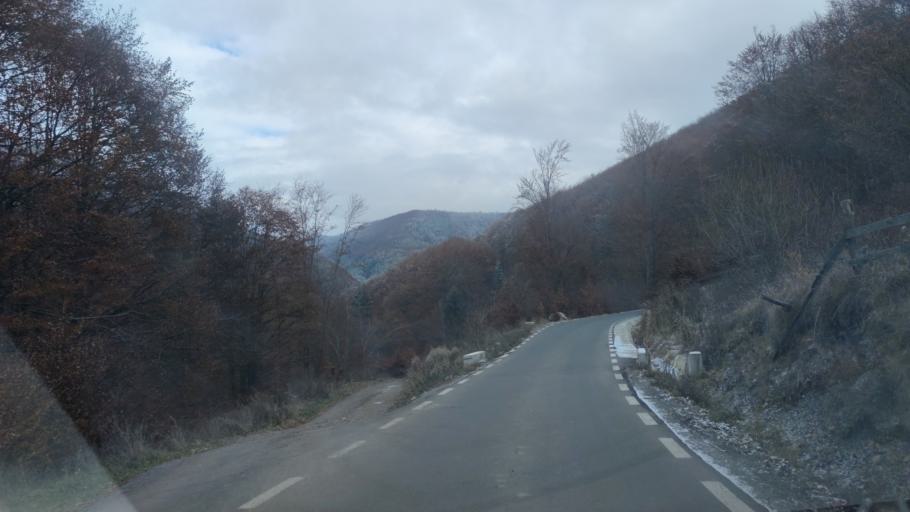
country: RO
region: Harghita
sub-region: Comuna Corund
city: Corund
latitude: 46.4816
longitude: 25.2231
